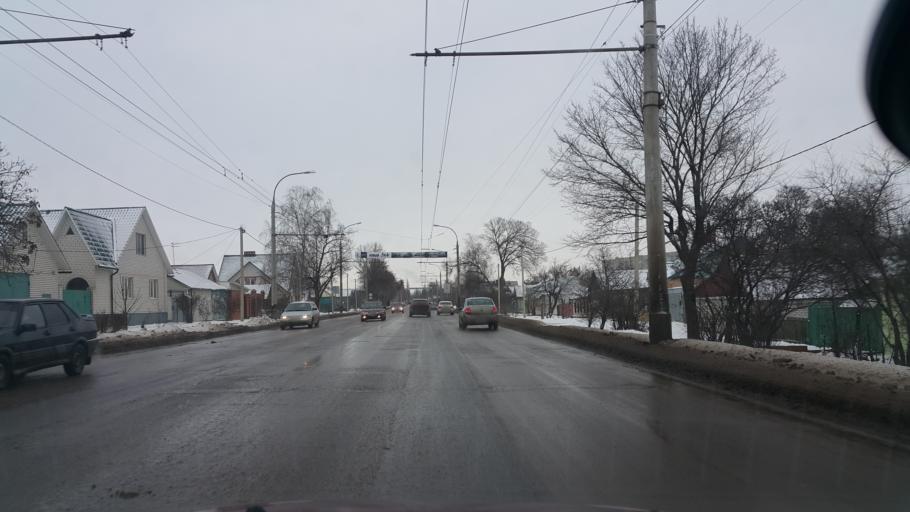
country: RU
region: Tambov
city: Tambov
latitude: 52.7275
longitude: 41.4029
